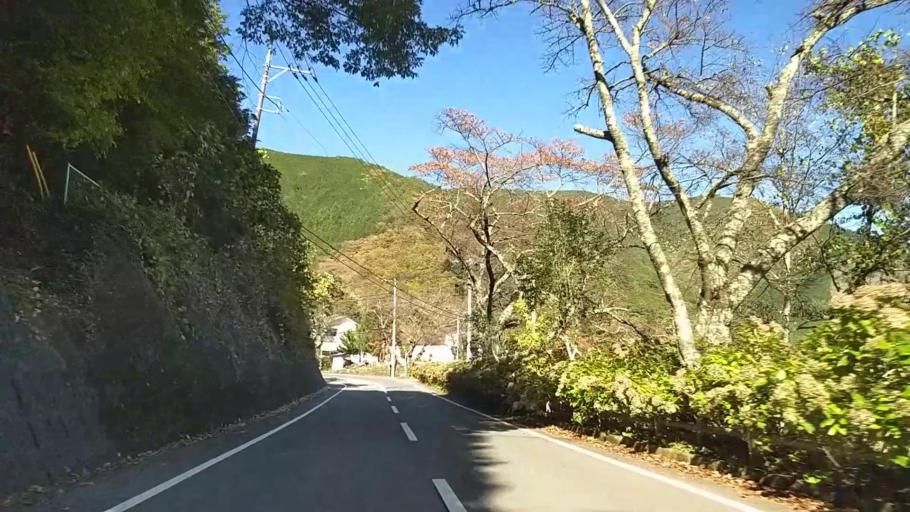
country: JP
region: Yamanashi
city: Otsuki
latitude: 35.7545
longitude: 138.9527
